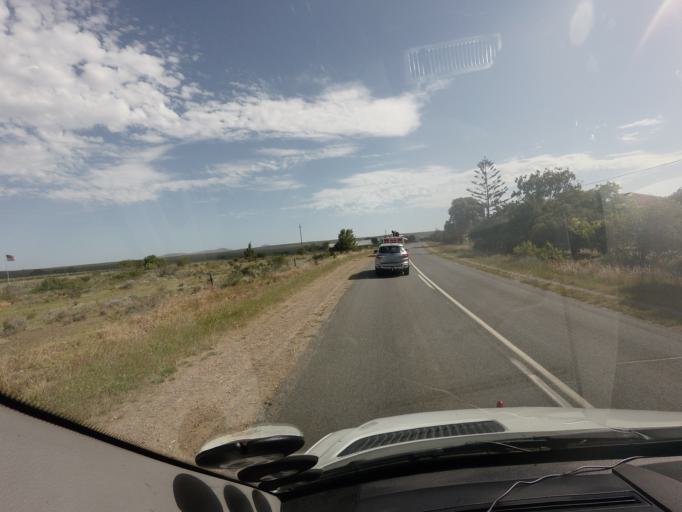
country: ZA
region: Western Cape
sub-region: Overberg District Municipality
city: Caledon
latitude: -34.4382
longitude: 19.4615
